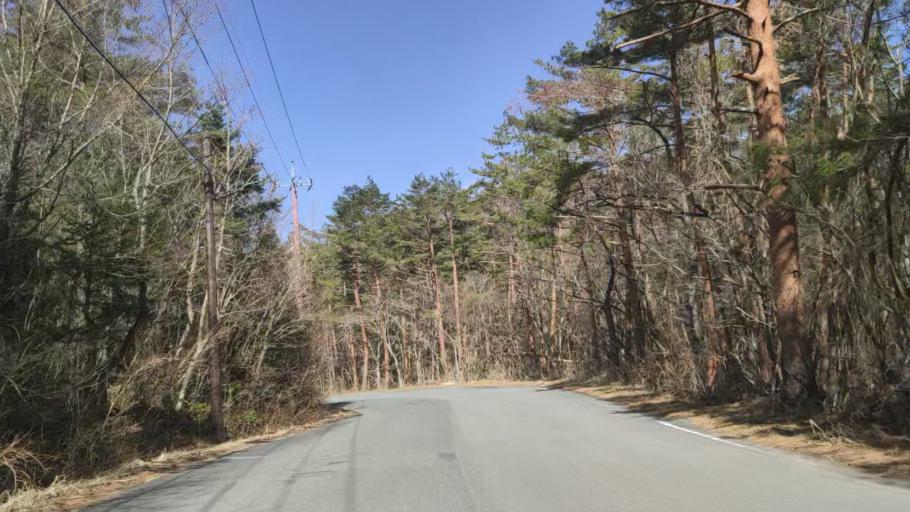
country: JP
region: Yamanashi
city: Fujikawaguchiko
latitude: 35.4964
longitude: 138.6666
